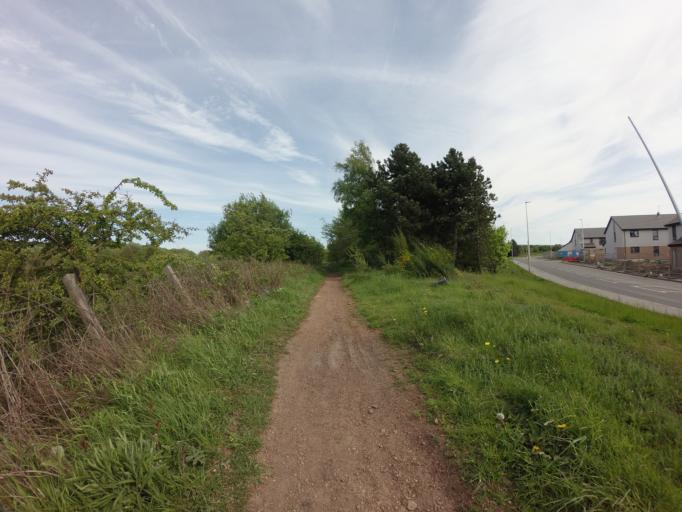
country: GB
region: Scotland
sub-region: West Lothian
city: Mid Calder
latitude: 55.9125
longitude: -3.4904
